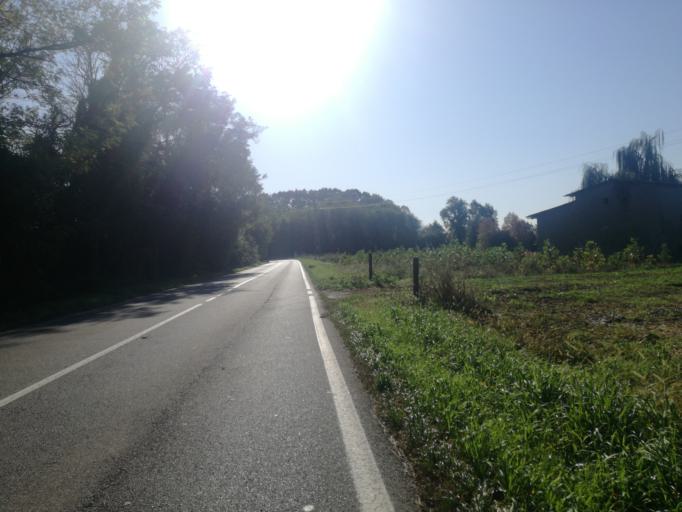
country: IT
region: Lombardy
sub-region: Provincia di Monza e Brianza
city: Cornate d'Adda
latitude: 45.6335
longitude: 9.4906
